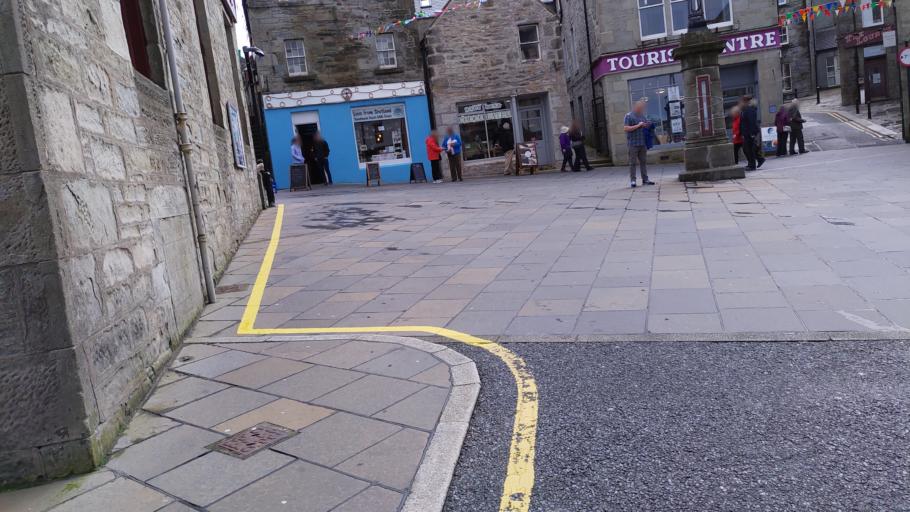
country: GB
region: Scotland
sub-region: Shetland Islands
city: Shetland
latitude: 60.1534
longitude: -1.1425
